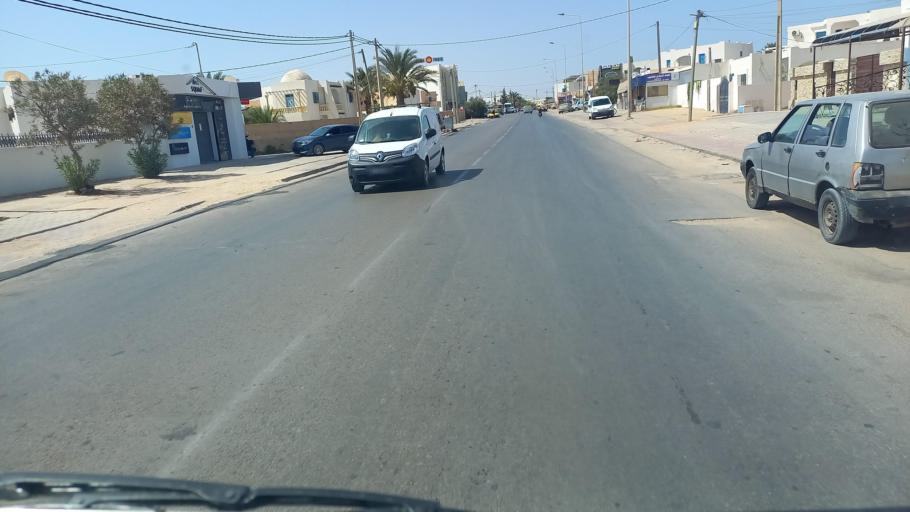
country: TN
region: Madanin
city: Houmt Souk
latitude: 33.8713
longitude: 10.8724
